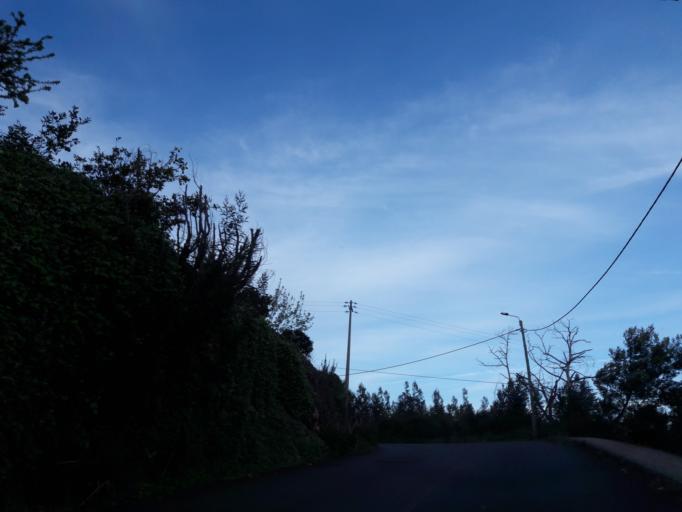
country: PT
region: Madeira
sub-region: Santa Cruz
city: Camacha
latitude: 32.6879
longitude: -16.8634
